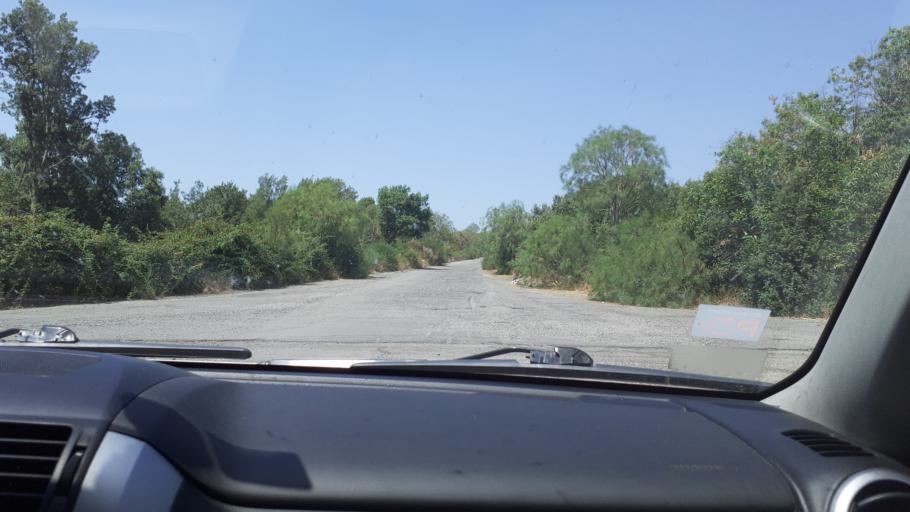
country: IT
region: Sicily
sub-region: Catania
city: Nicolosi
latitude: 37.6469
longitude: 15.0134
